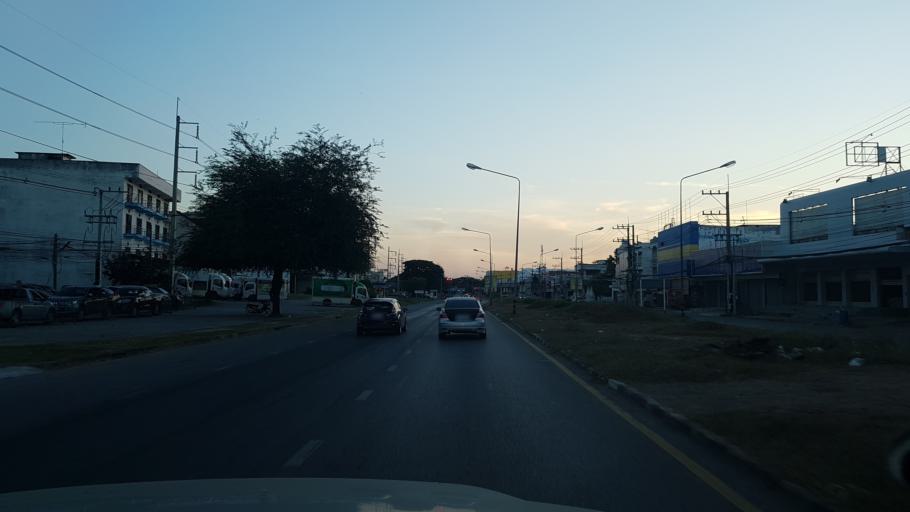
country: TH
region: Khon Kaen
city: Chum Phae
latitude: 16.5390
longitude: 102.1074
